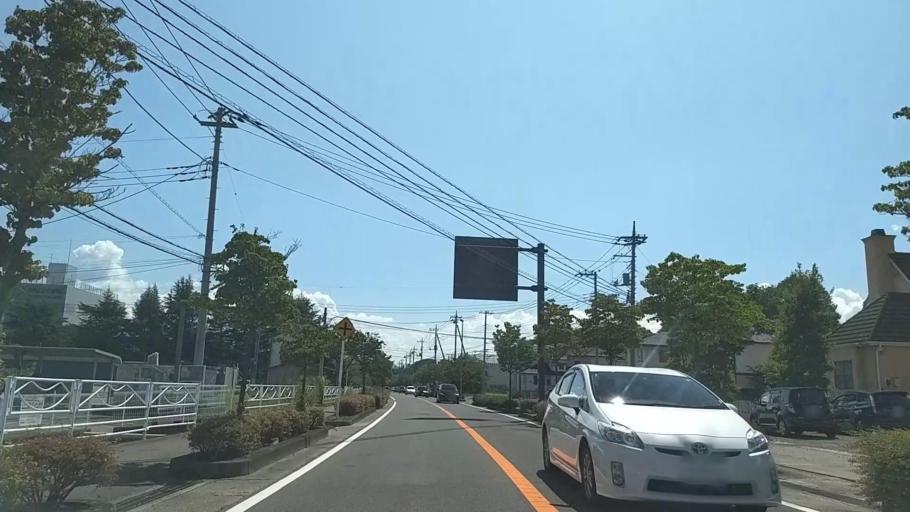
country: JP
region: Yamanashi
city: Ryuo
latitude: 35.6339
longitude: 138.4986
